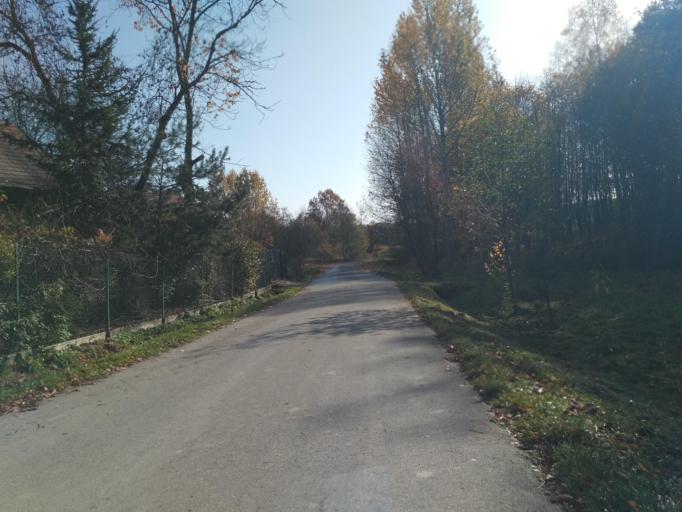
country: PL
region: Subcarpathian Voivodeship
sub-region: Powiat rzeszowski
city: Blazowa
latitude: 49.8620
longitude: 22.1251
